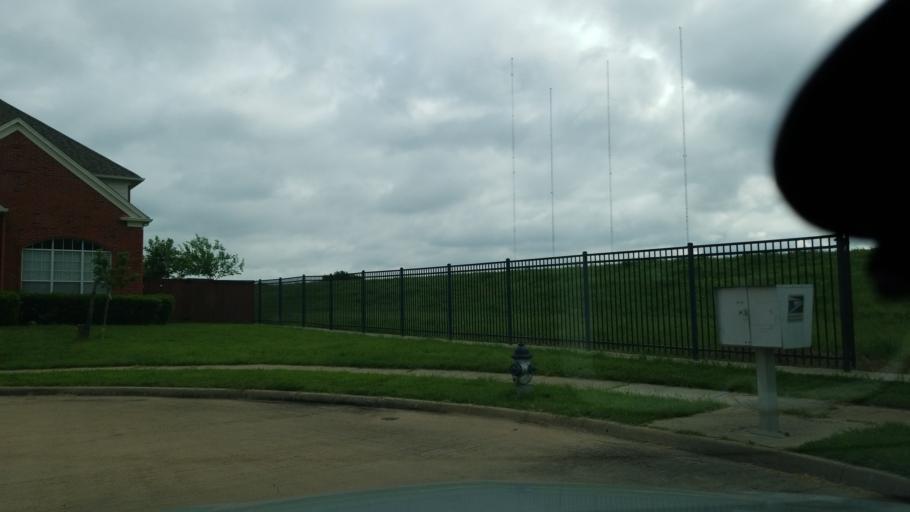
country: US
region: Texas
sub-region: Dallas County
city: Farmers Branch
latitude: 32.9416
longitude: -96.9431
